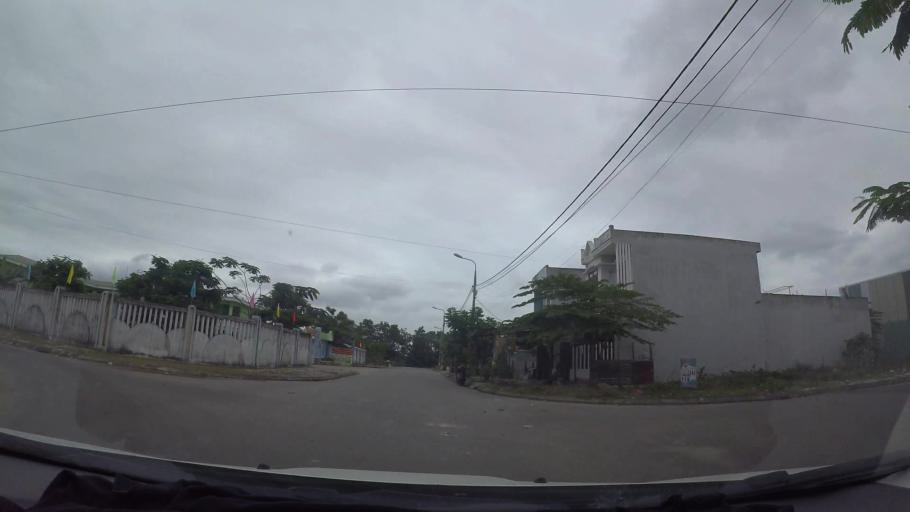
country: VN
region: Da Nang
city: Lien Chieu
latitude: 16.0954
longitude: 108.1034
